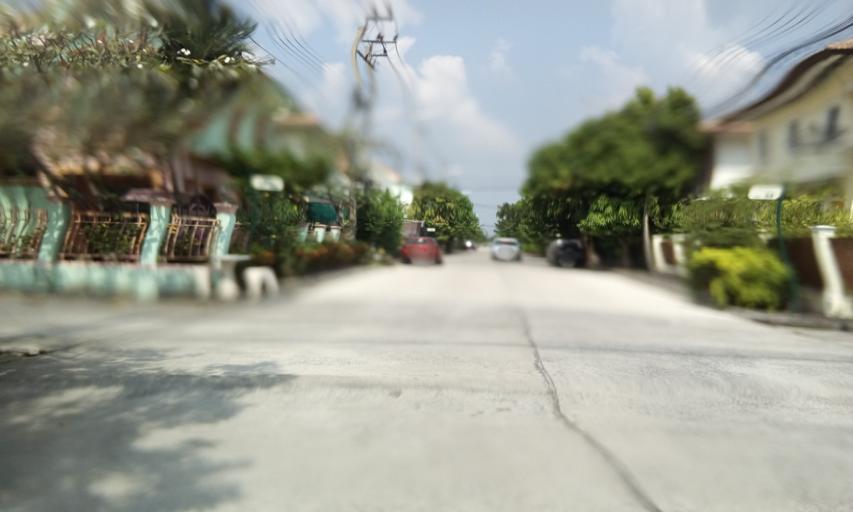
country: TH
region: Pathum Thani
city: Ban Rangsit
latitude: 14.0424
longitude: 100.7653
